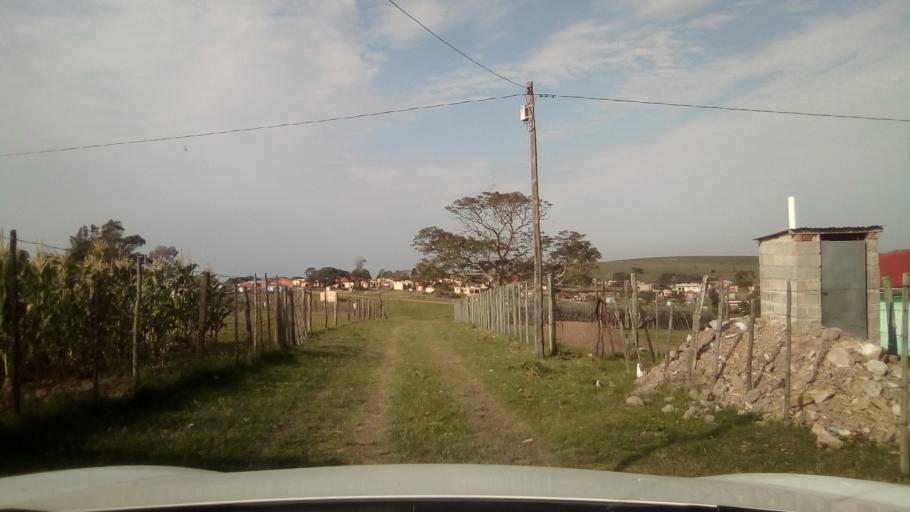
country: ZA
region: Eastern Cape
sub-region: Buffalo City Metropolitan Municipality
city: Bhisho
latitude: -33.0065
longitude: 27.3024
